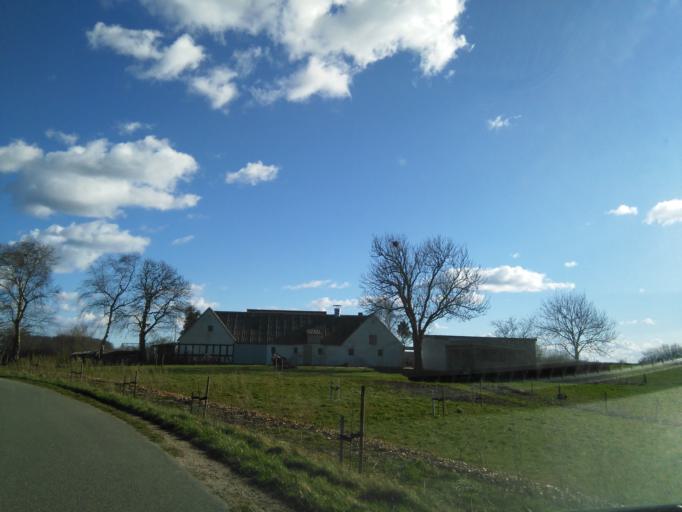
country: DK
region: Central Jutland
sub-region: Arhus Kommune
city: Beder
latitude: 56.0647
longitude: 10.2335
